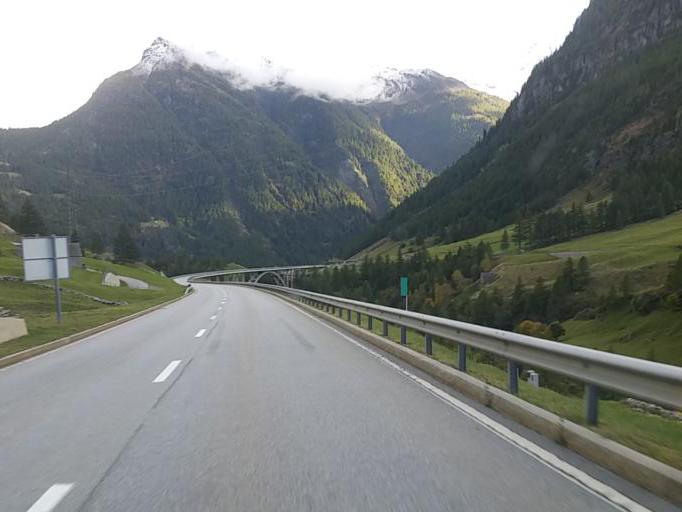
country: CH
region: Valais
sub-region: Brig District
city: Brig
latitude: 46.1971
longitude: 8.0601
